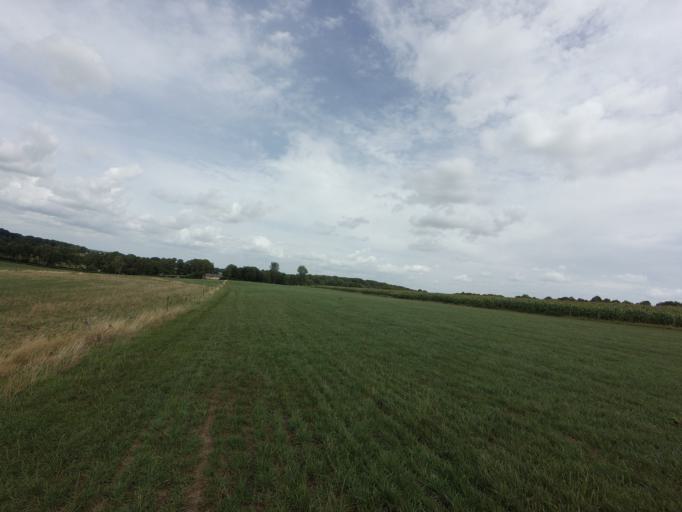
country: NL
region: Limburg
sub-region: Valkenburg aan de Geul
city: Schin op Geul
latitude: 50.7895
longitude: 5.8867
